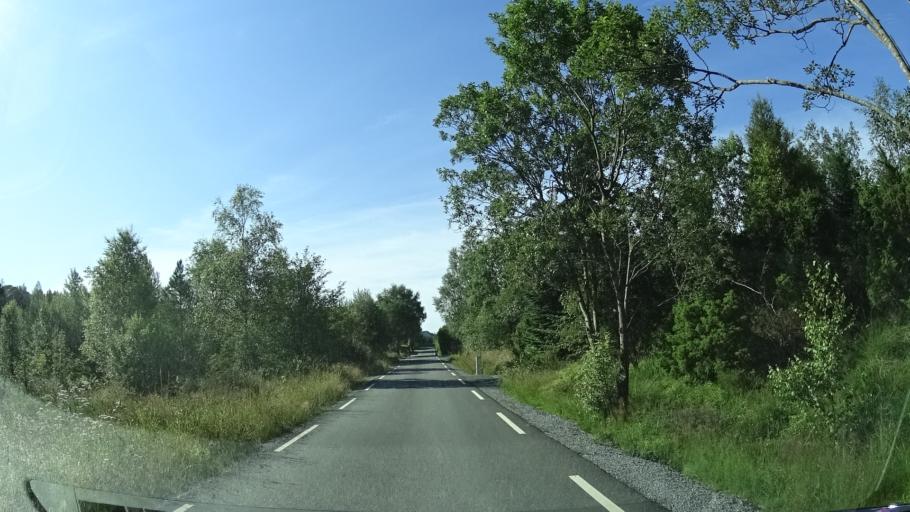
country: NO
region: Hordaland
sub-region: Fitjar
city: Fitjar
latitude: 59.9009
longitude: 5.2960
